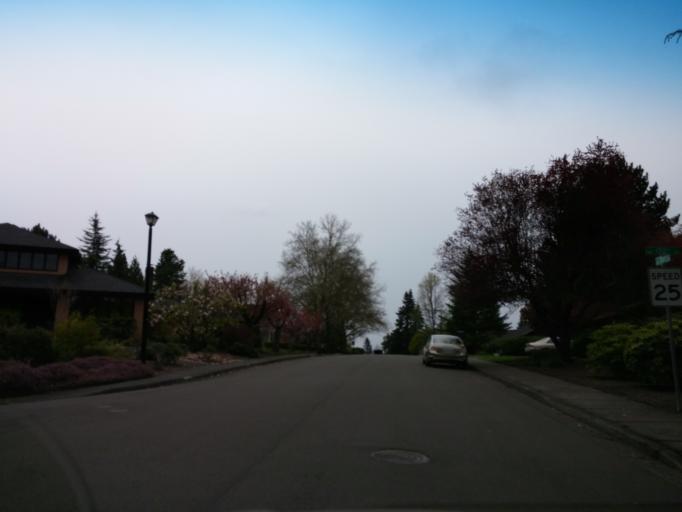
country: US
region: Oregon
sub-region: Washington County
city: Oak Hills
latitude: 45.5247
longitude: -122.8525
